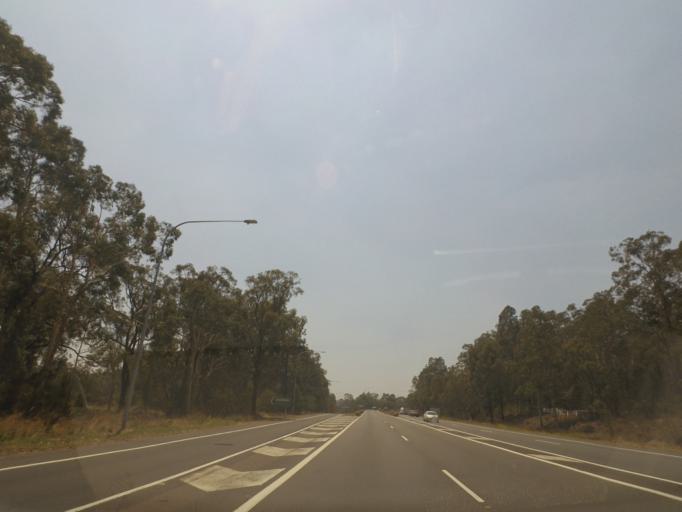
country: AU
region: New South Wales
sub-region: Newcastle
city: Beresfield
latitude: -32.8107
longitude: 151.6440
